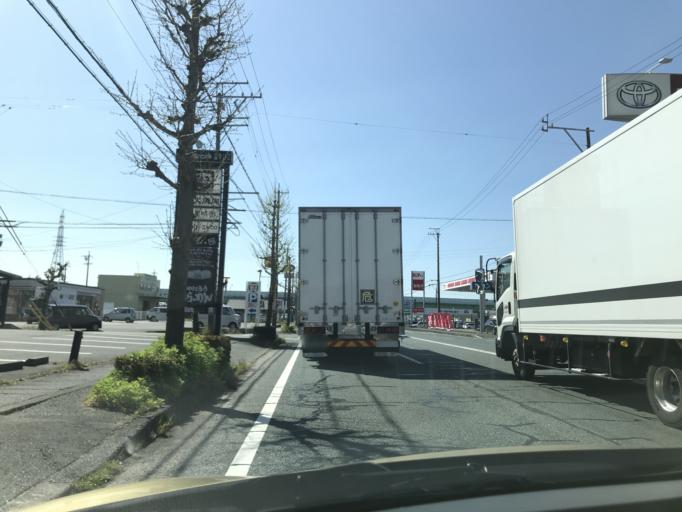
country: JP
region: Shizuoka
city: Fukuroi
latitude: 34.7545
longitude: 137.9075
